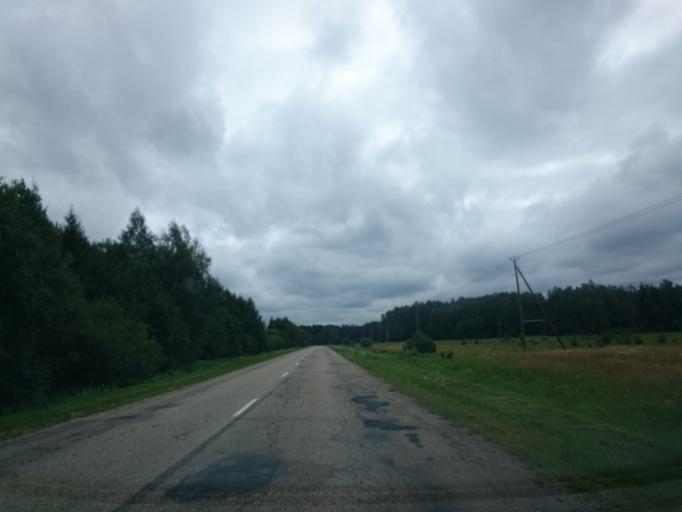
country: LV
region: Pavilostas
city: Pavilosta
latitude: 56.8124
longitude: 21.2260
